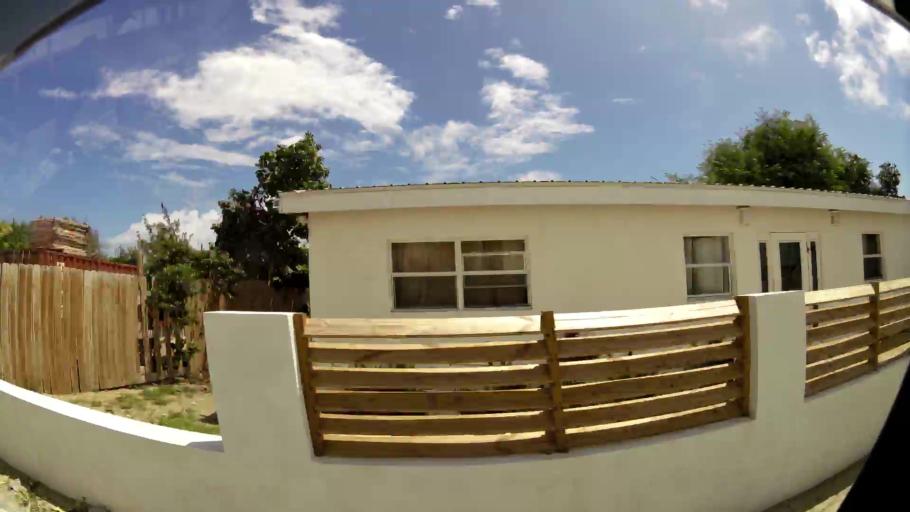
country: TC
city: Cockburn Town
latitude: 21.4742
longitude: -71.1482
